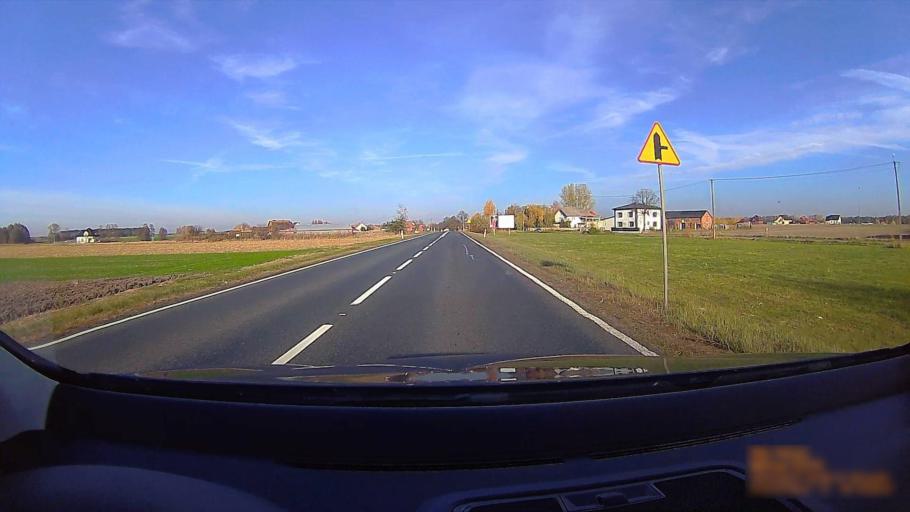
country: PL
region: Greater Poland Voivodeship
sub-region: Powiat koninski
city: Rychwal
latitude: 52.1253
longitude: 18.1743
